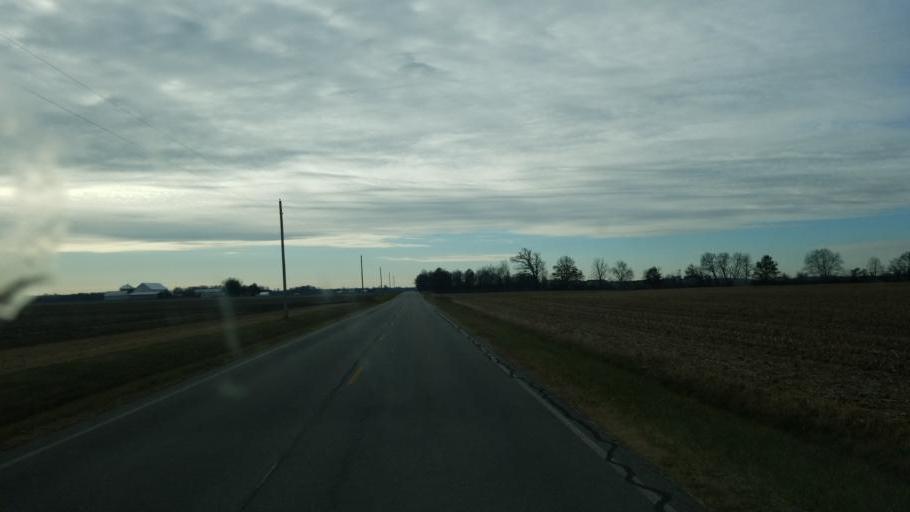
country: US
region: Ohio
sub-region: Marion County
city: Marion
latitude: 40.5965
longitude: -83.0101
